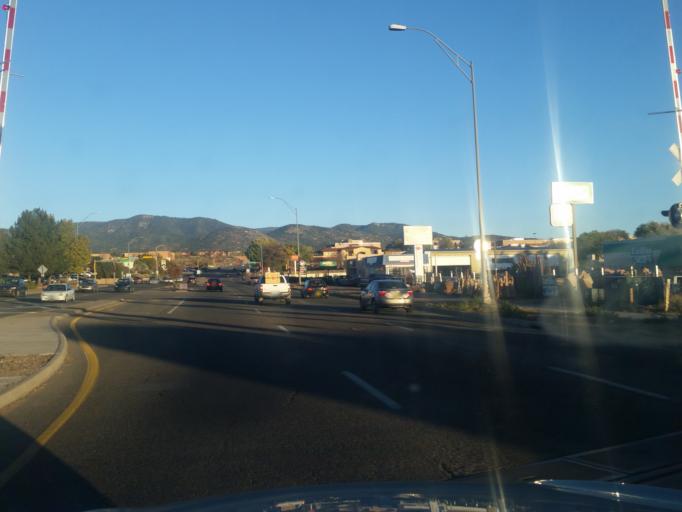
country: US
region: New Mexico
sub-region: Santa Fe County
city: Santa Fe
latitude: 35.6594
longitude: -105.9655
